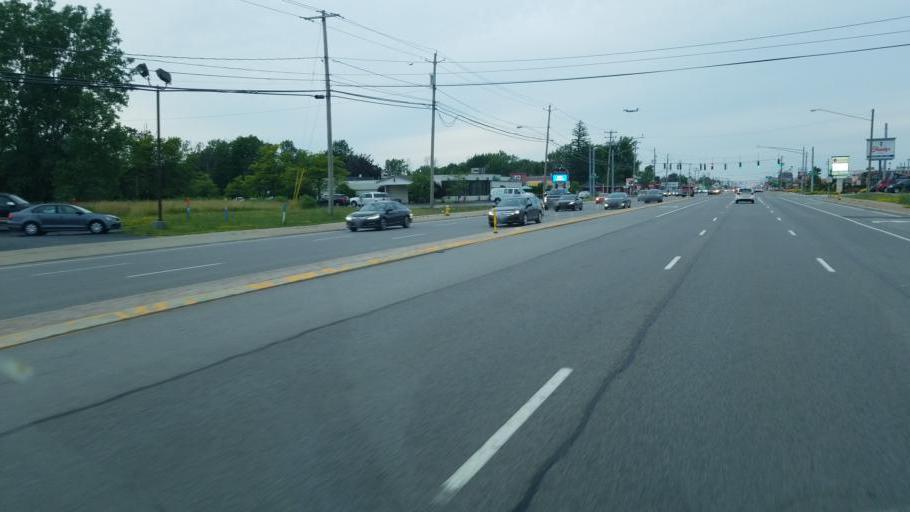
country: US
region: New York
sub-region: Erie County
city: Harris Hill
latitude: 42.9510
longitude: -78.6968
